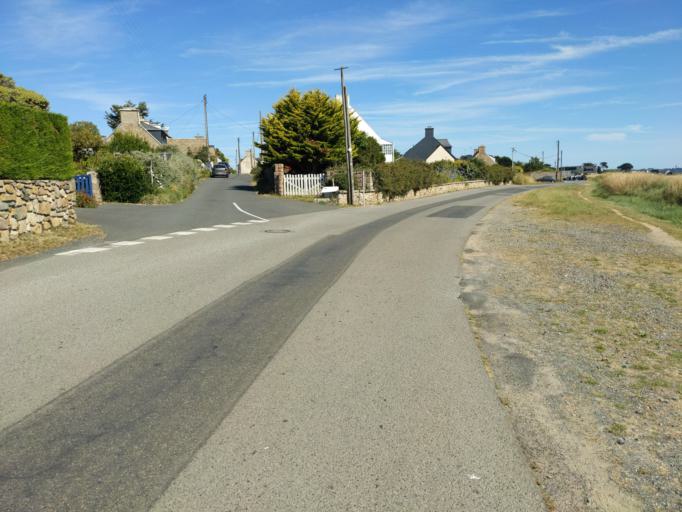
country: FR
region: Brittany
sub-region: Departement des Cotes-d'Armor
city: Pleubian
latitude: 48.8631
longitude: -3.0848
